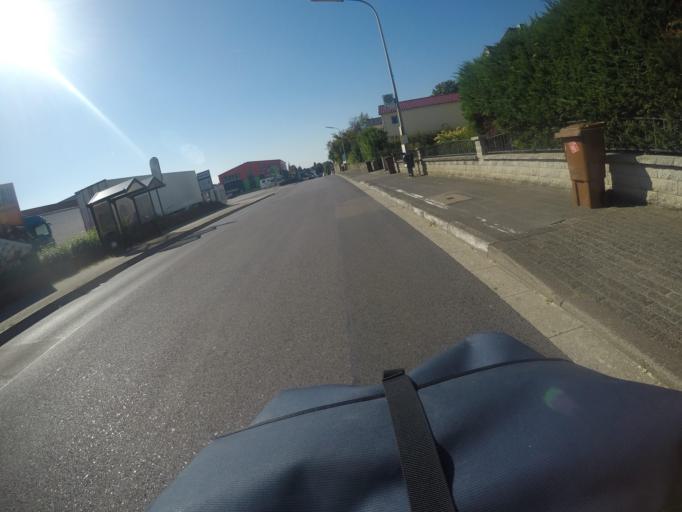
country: DE
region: North Rhine-Westphalia
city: Leichlingen
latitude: 51.1063
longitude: 6.9992
